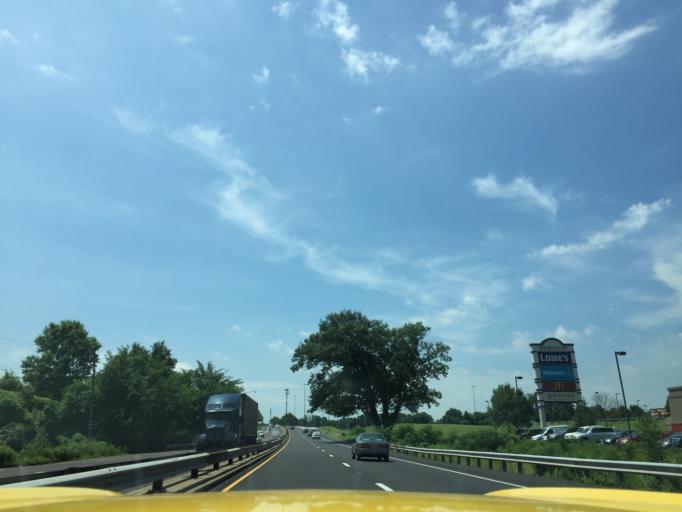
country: US
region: Pennsylvania
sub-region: Bucks County
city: Trevose
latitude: 40.1364
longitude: -74.9630
